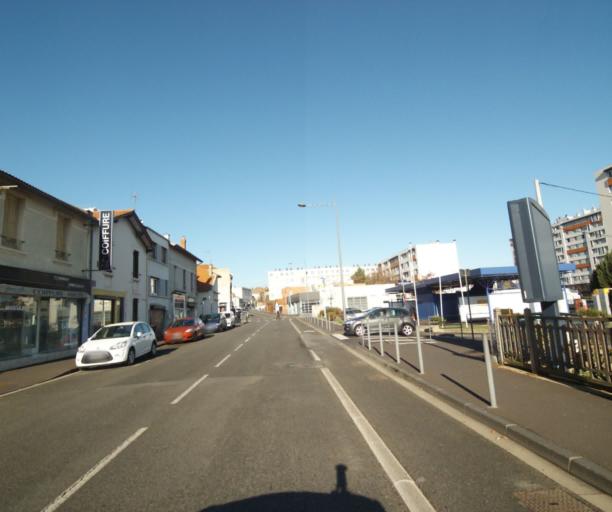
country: FR
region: Auvergne
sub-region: Departement du Puy-de-Dome
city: Aubiere
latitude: 45.7641
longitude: 3.0983
